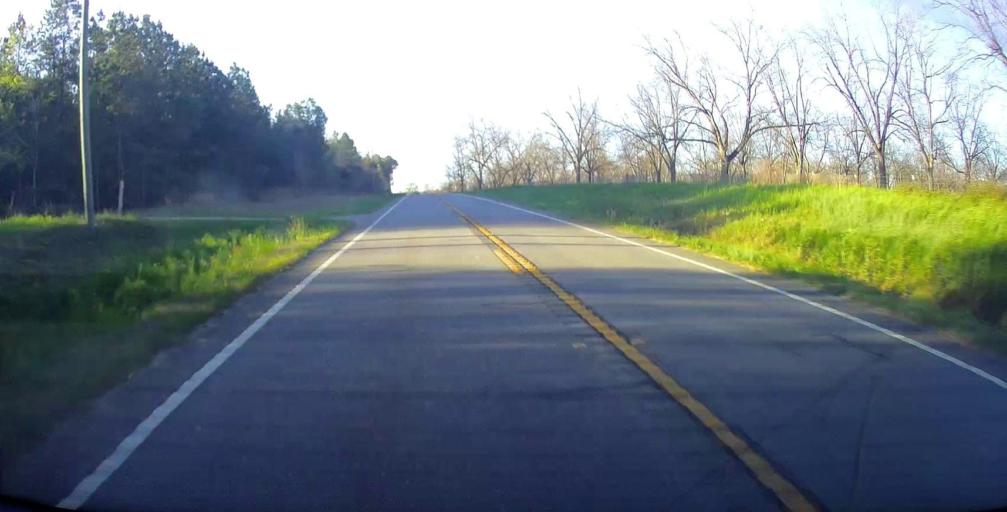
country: US
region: Georgia
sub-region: Wilcox County
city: Abbeville
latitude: 32.0307
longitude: -83.2512
